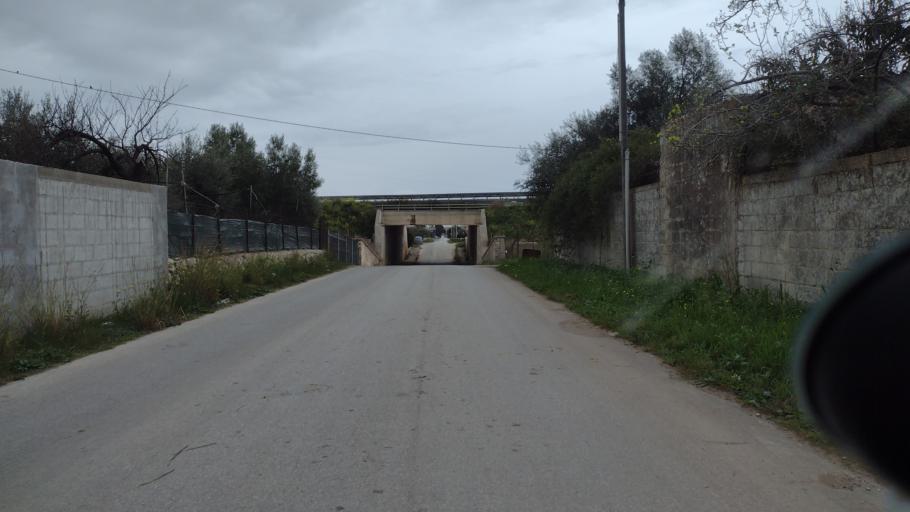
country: IT
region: Sicily
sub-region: Provincia di Siracusa
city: Avola
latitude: 36.9111
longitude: 15.1194
